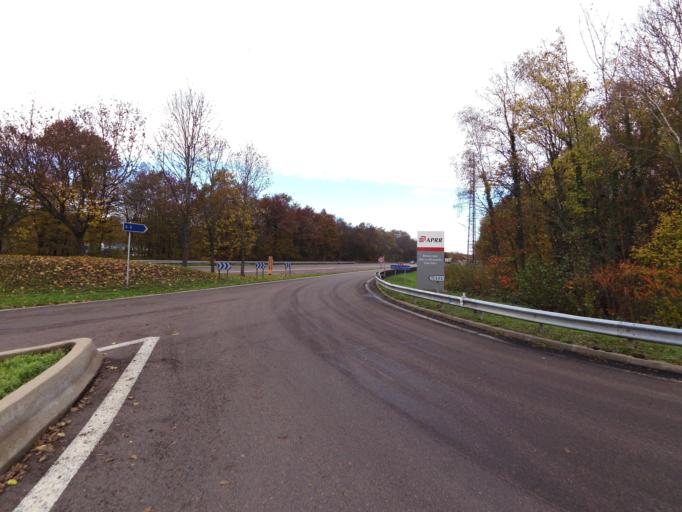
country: FR
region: Bourgogne
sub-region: Departement de Saone-et-Loire
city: Champforgeuil
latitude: 46.8618
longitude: 4.8230
